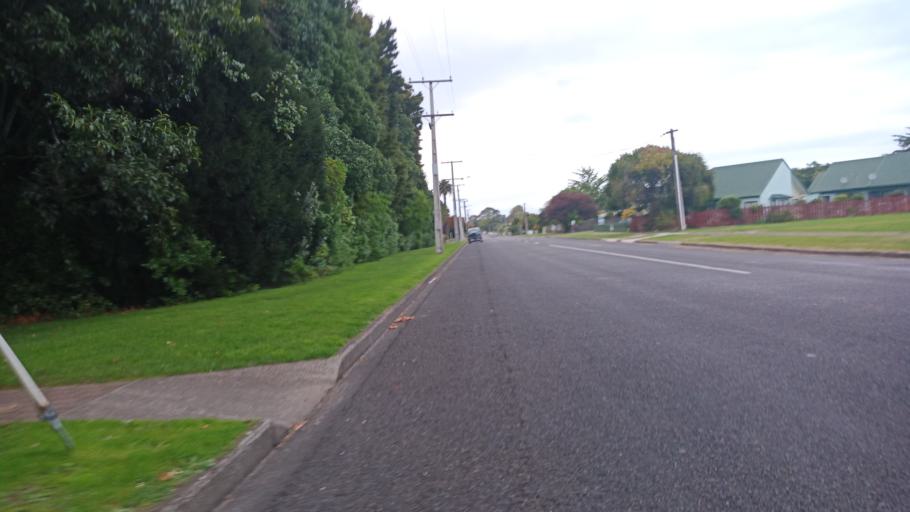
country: NZ
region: Gisborne
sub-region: Gisborne District
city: Gisborne
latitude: -38.6571
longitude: 178.0205
